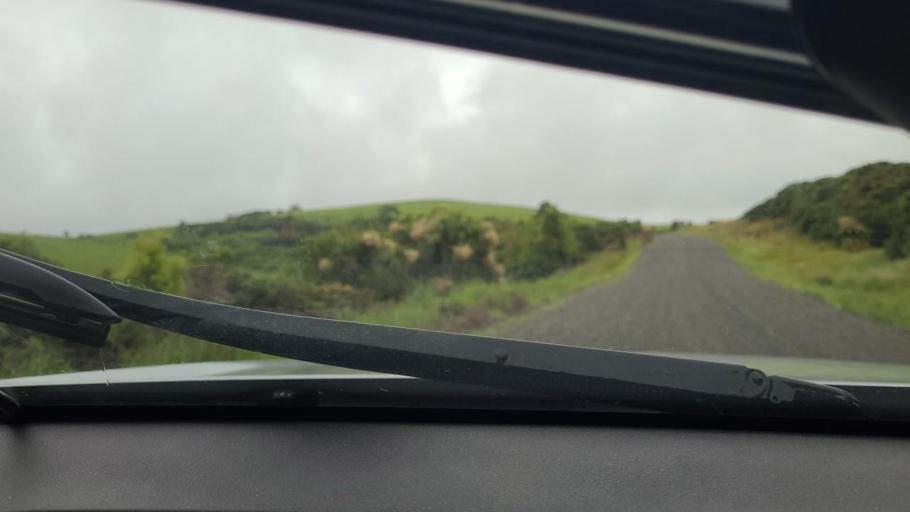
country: NZ
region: Southland
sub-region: Southland District
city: Riverton
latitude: -46.2120
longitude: 168.0305
